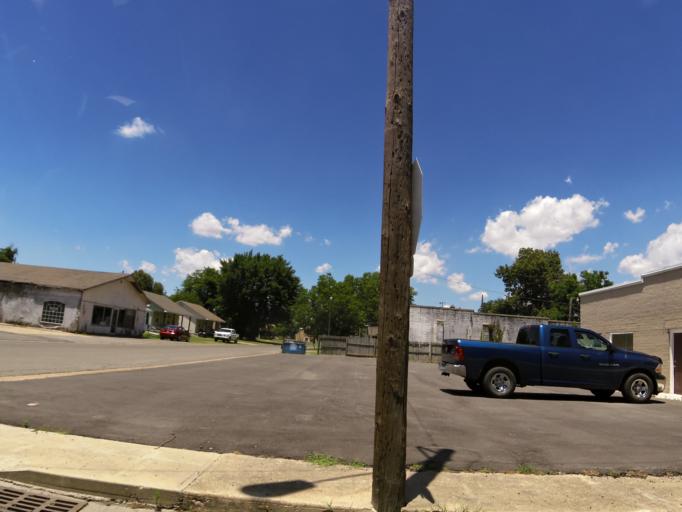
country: US
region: Missouri
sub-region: New Madrid County
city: New Madrid
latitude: 36.5851
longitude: -89.5280
